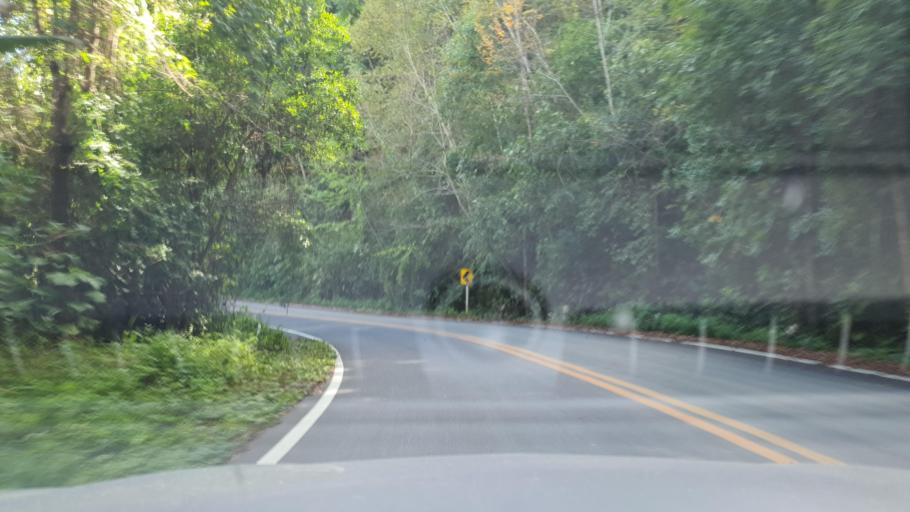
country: TH
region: Chiang Rai
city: Wiang Pa Pao
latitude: 19.3043
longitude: 99.3605
